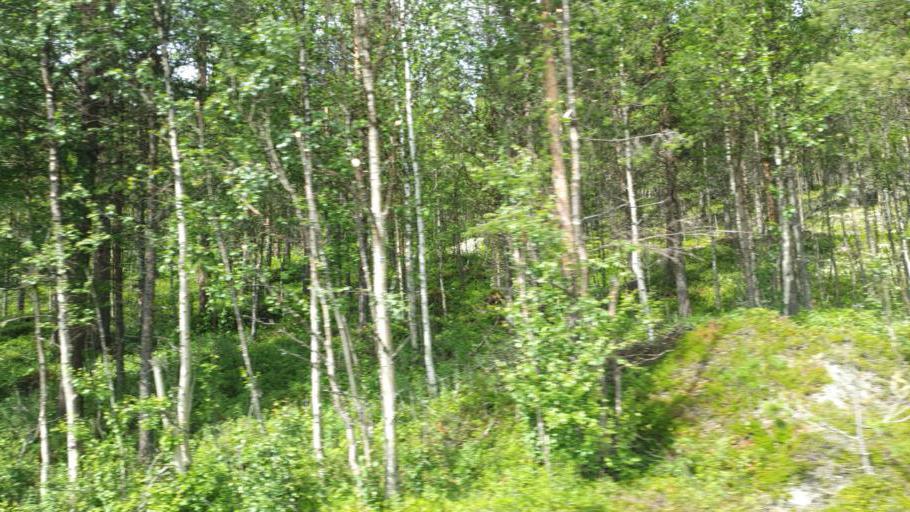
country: NO
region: Oppland
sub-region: Vaga
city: Vagamo
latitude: 61.6784
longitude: 9.0497
